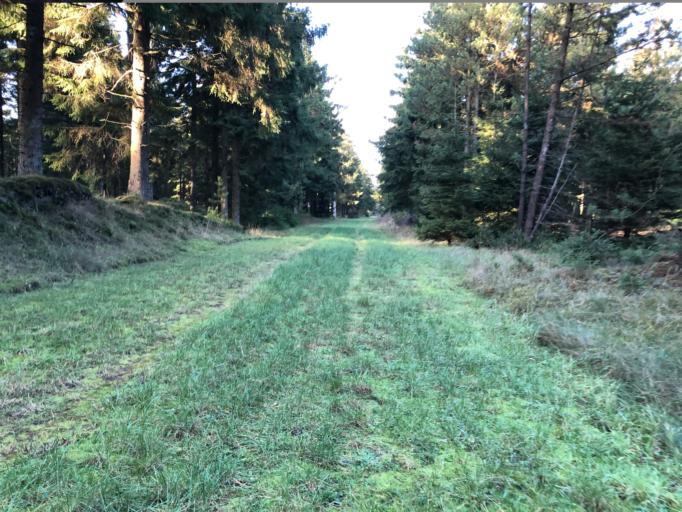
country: DK
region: Central Jutland
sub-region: Holstebro Kommune
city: Ulfborg
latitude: 56.2684
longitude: 8.3788
